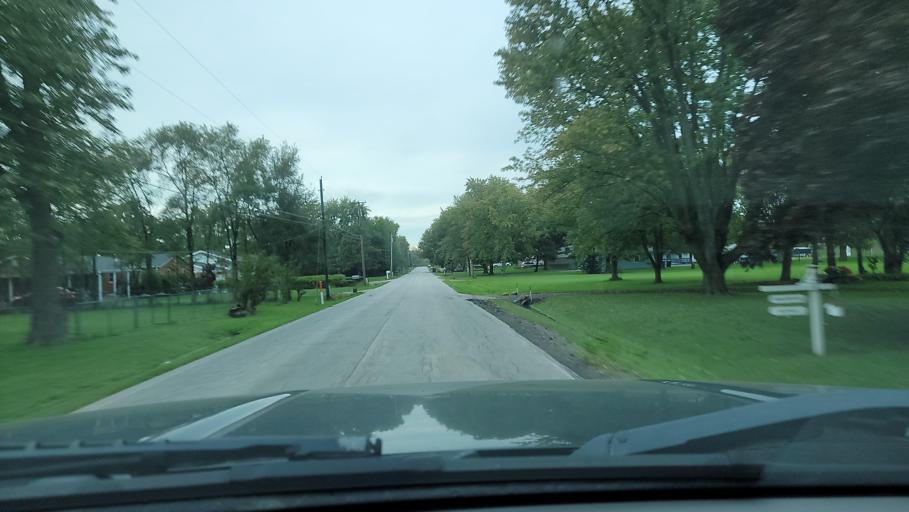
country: US
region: Indiana
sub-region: Porter County
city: South Haven
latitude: 41.5538
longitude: -87.1532
